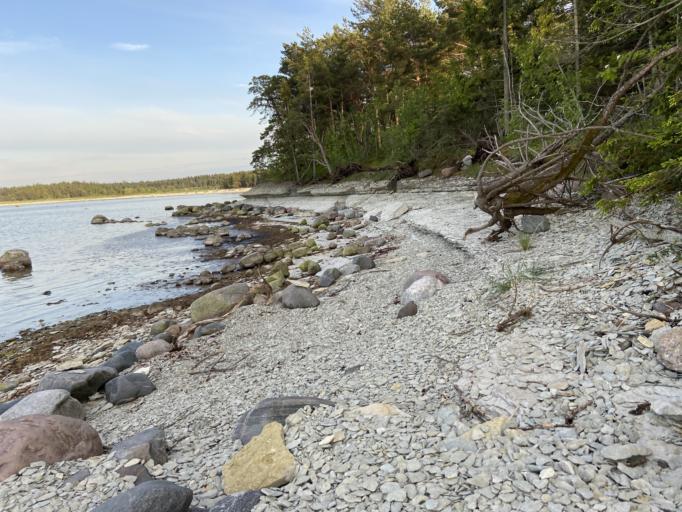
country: EE
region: Harju
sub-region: Paldiski linn
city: Paldiski
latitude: 59.2731
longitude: 23.7339
